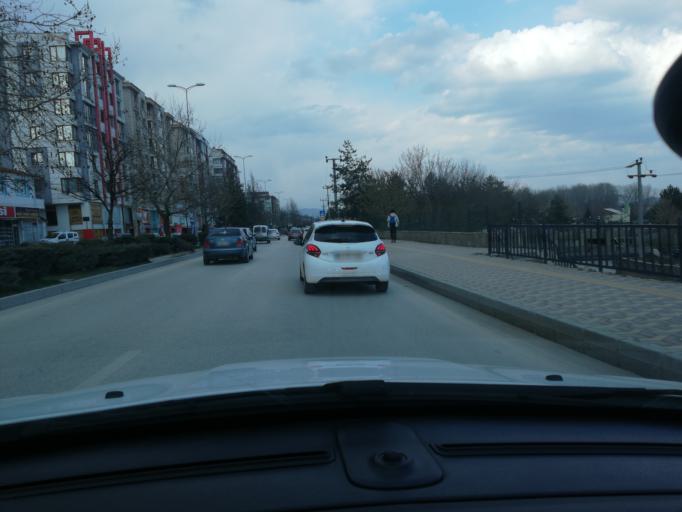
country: TR
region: Kastamonu
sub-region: Cide
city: Kastamonu
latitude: 41.4034
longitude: 33.7836
